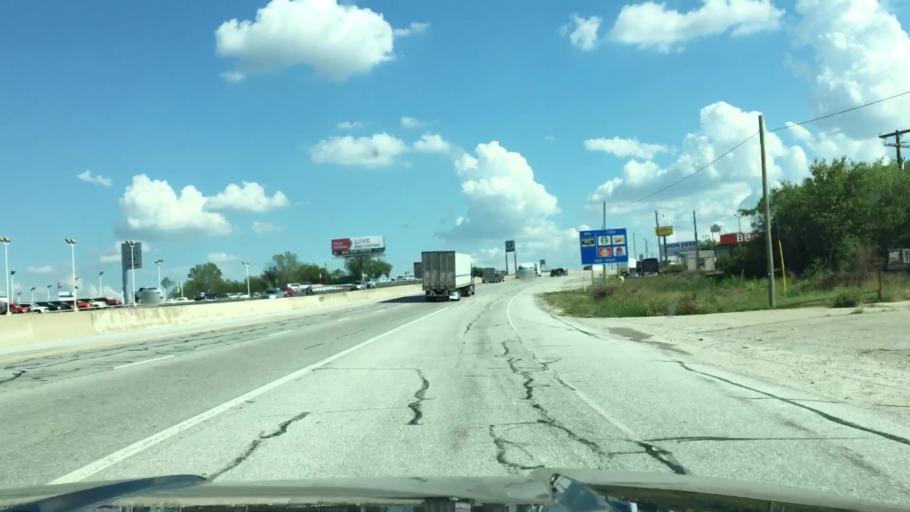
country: US
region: Texas
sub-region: Wise County
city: Decatur
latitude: 33.2384
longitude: -97.5989
